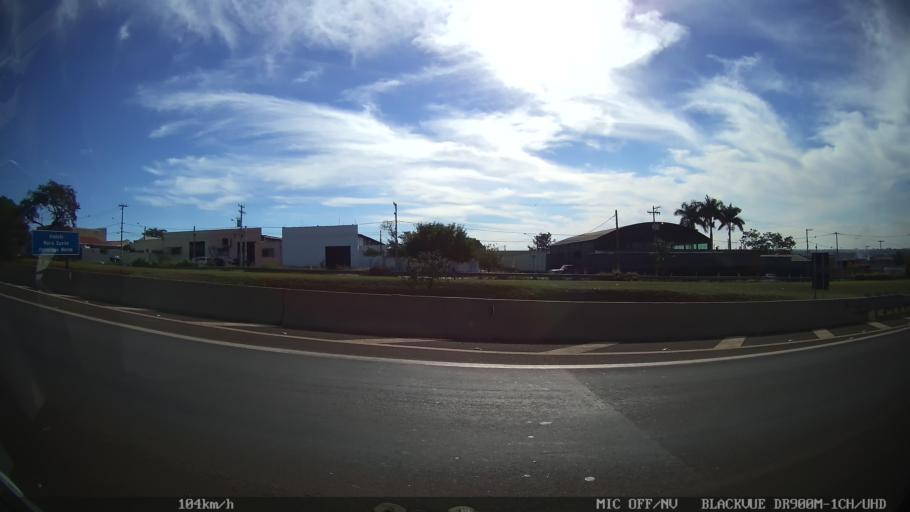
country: BR
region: Sao Paulo
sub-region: Araraquara
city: Araraquara
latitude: -21.8092
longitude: -48.1535
